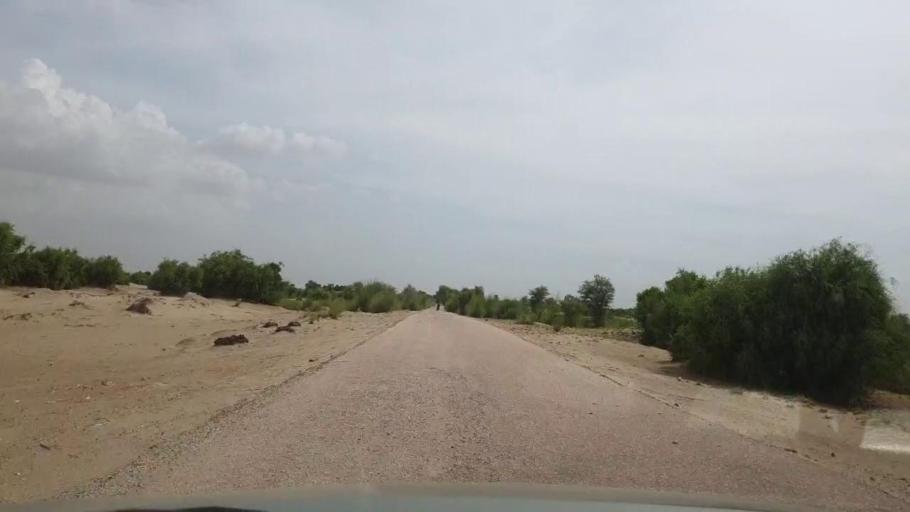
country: PK
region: Sindh
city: Kot Diji
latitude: 27.1221
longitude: 69.0264
